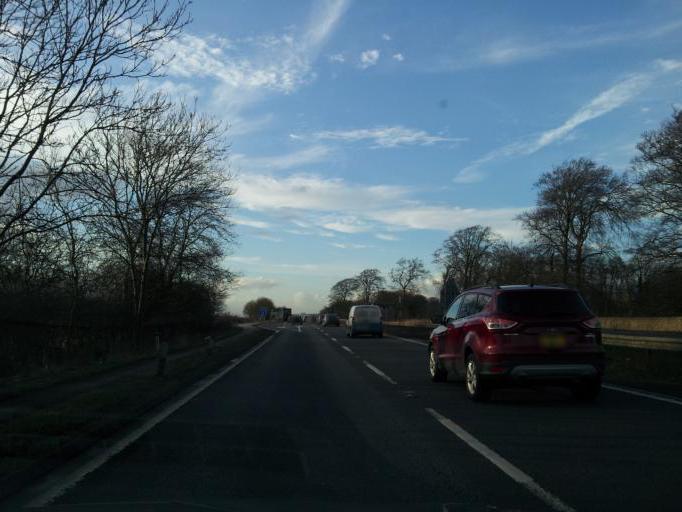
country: GB
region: England
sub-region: Peterborough
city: Wittering
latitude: 52.6260
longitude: -0.4642
